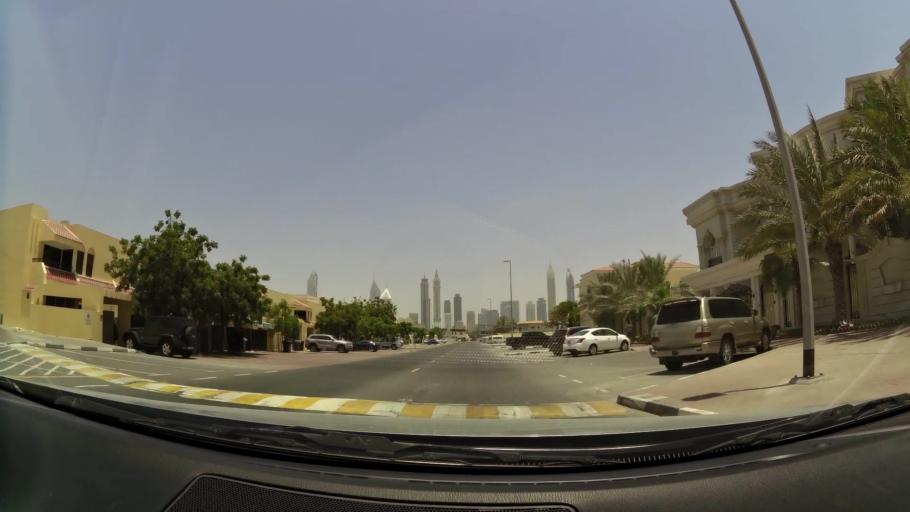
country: AE
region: Dubai
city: Dubai
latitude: 25.2256
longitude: 55.2629
